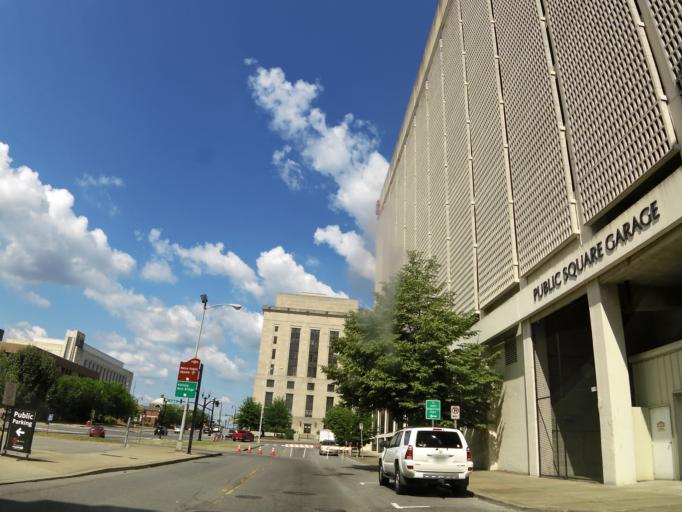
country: US
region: Tennessee
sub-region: Davidson County
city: Nashville
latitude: 36.1665
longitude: -86.7803
